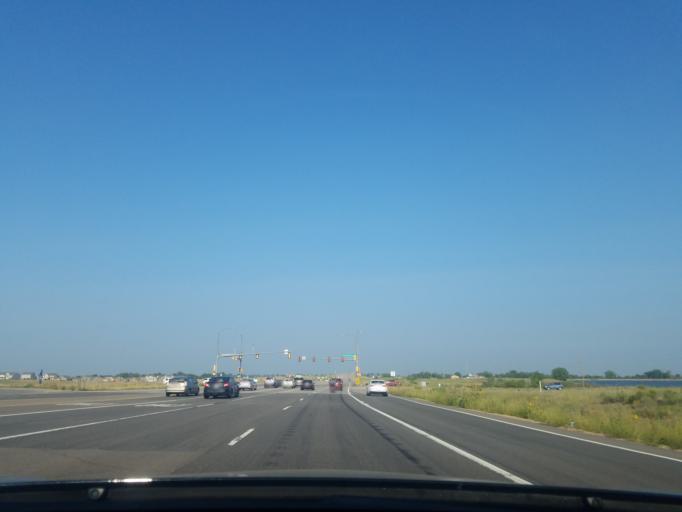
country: US
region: Colorado
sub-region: Larimer County
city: Campion
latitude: 40.3357
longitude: -105.0950
